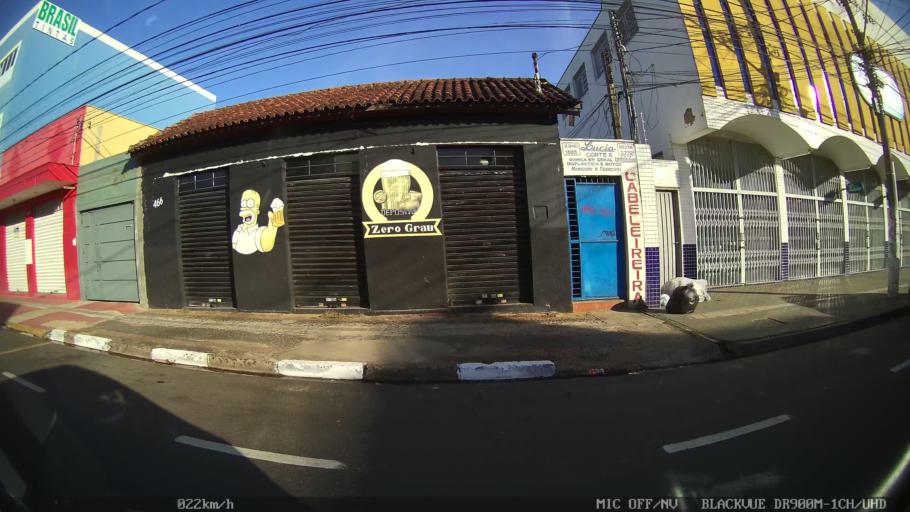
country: BR
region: Sao Paulo
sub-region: Franca
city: Franca
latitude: -20.5272
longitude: -47.3876
